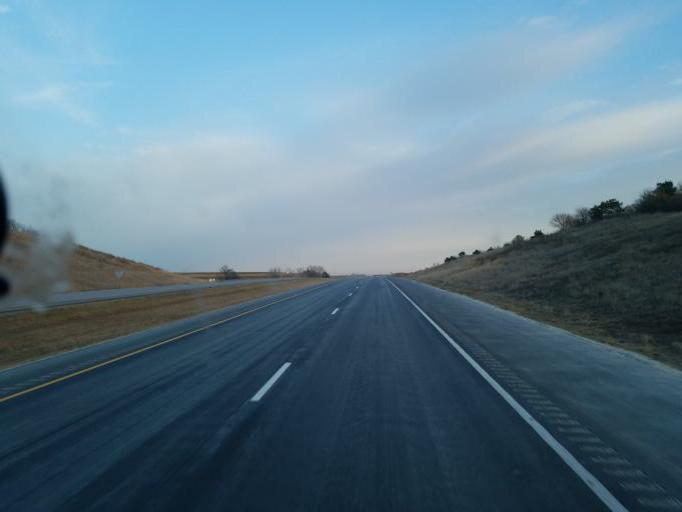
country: US
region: Iowa
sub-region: Harrison County
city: Missouri Valley
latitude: 41.4986
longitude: -95.7530
